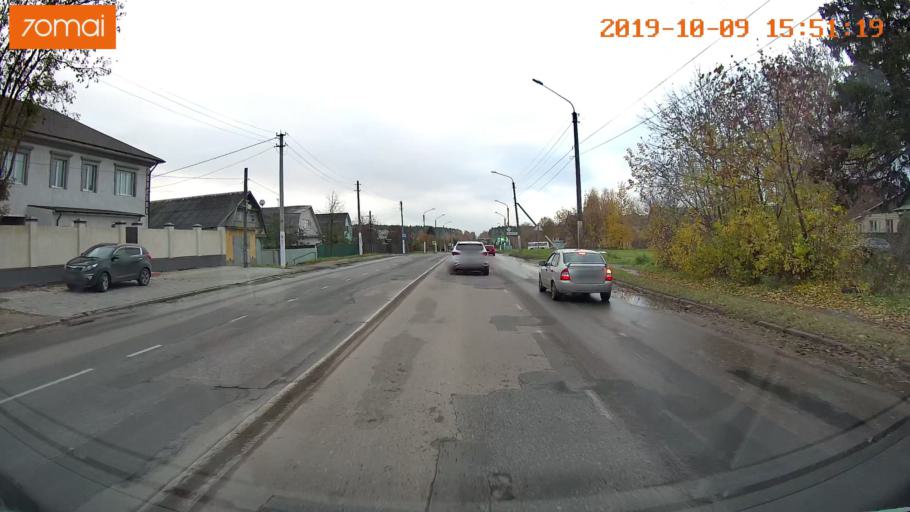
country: RU
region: Kostroma
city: Oktyabr'skiy
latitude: 57.7982
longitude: 40.9803
